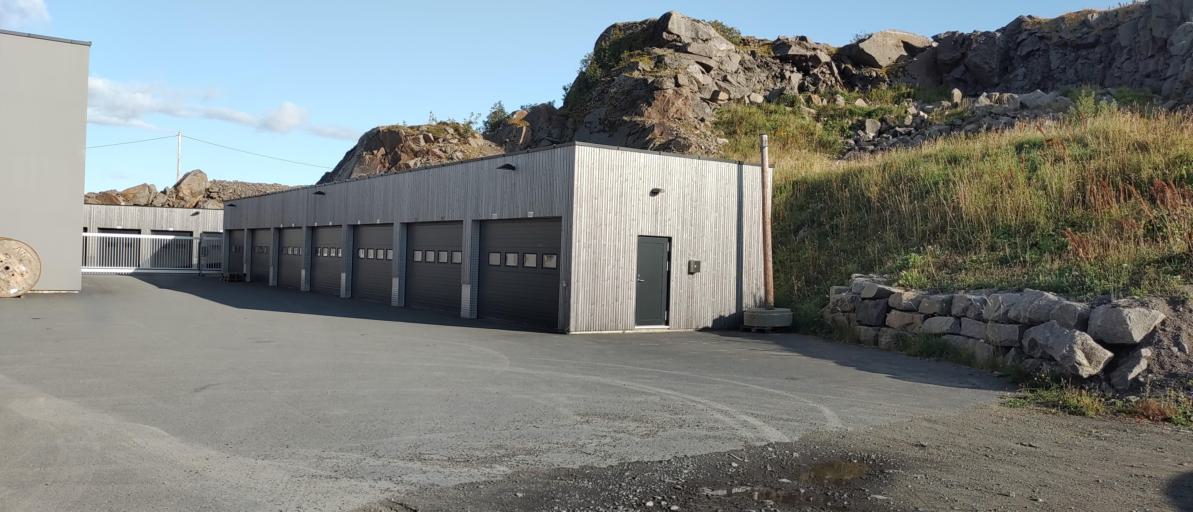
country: NO
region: Nordland
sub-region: Vagan
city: Svolvaer
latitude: 68.2249
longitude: 14.5558
